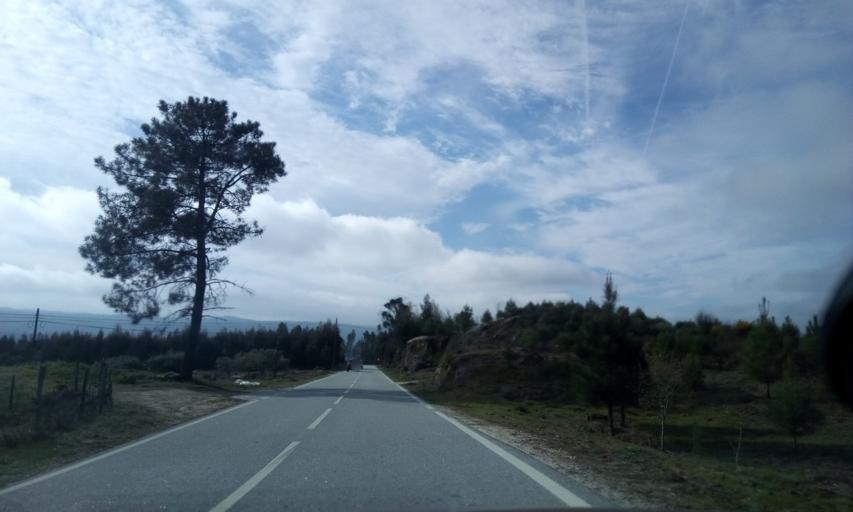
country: PT
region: Guarda
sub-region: Aguiar da Beira
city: Aguiar da Beira
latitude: 40.7495
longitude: -7.5497
